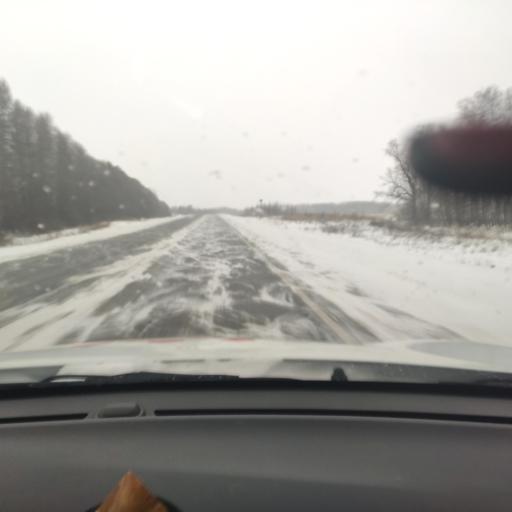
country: RU
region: Tatarstan
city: Verkhniy Uslon
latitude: 55.6817
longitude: 48.8707
